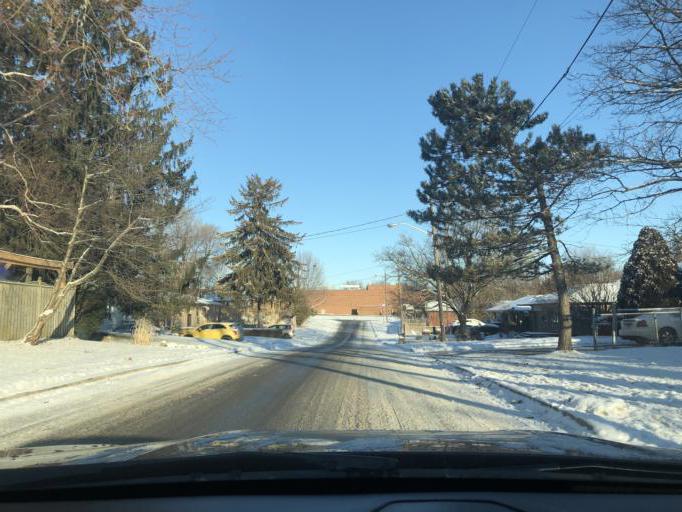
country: CA
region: Ontario
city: Pickering
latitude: 43.7871
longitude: -79.1388
